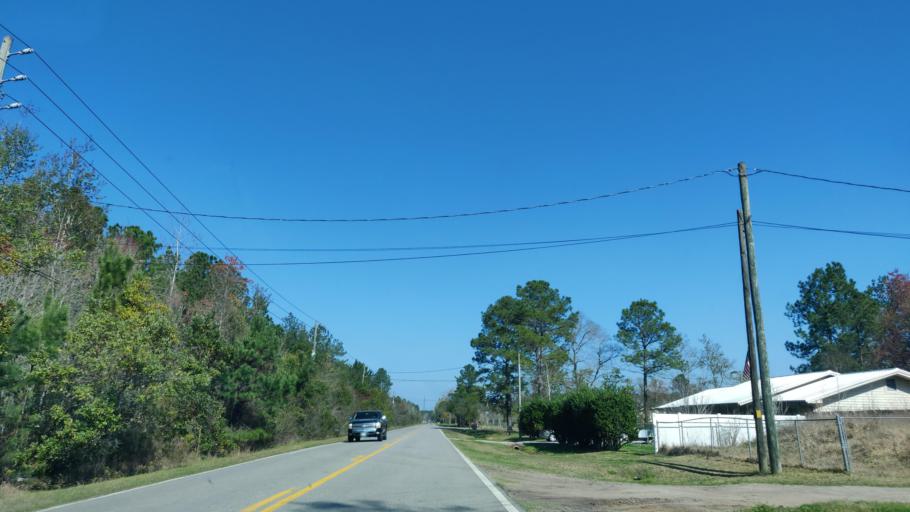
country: US
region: Florida
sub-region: Duval County
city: Baldwin
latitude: 30.2754
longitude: -81.9606
